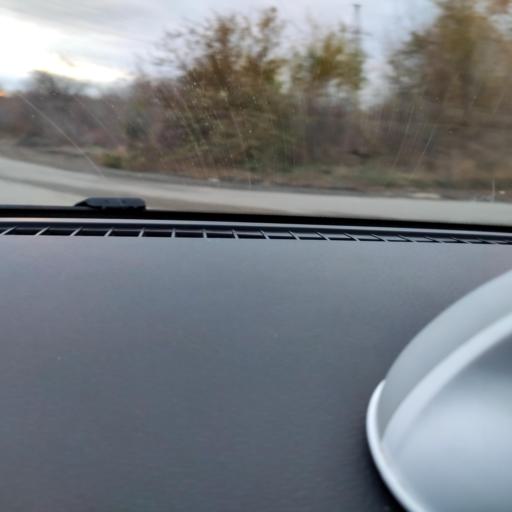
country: RU
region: Samara
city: Petra-Dubrava
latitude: 53.2603
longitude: 50.2909
